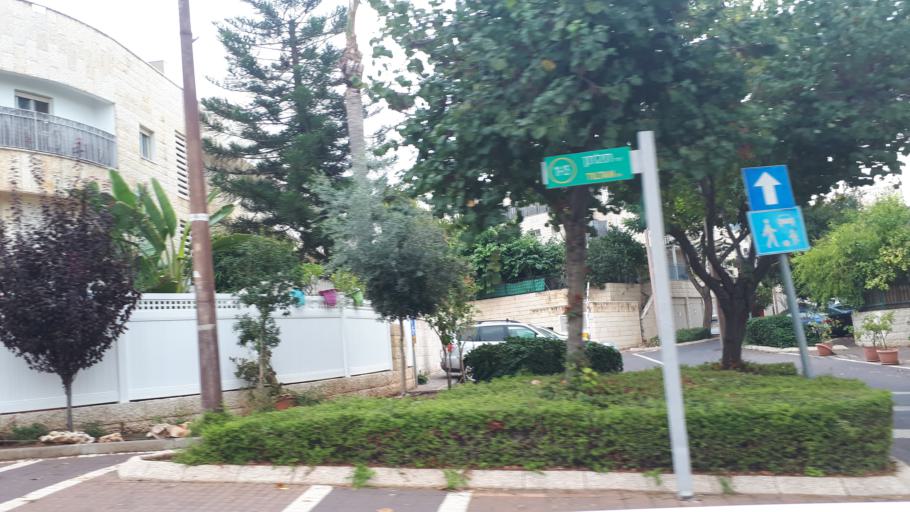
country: IL
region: Central District
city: Modiin
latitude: 31.9052
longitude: 35.0079
